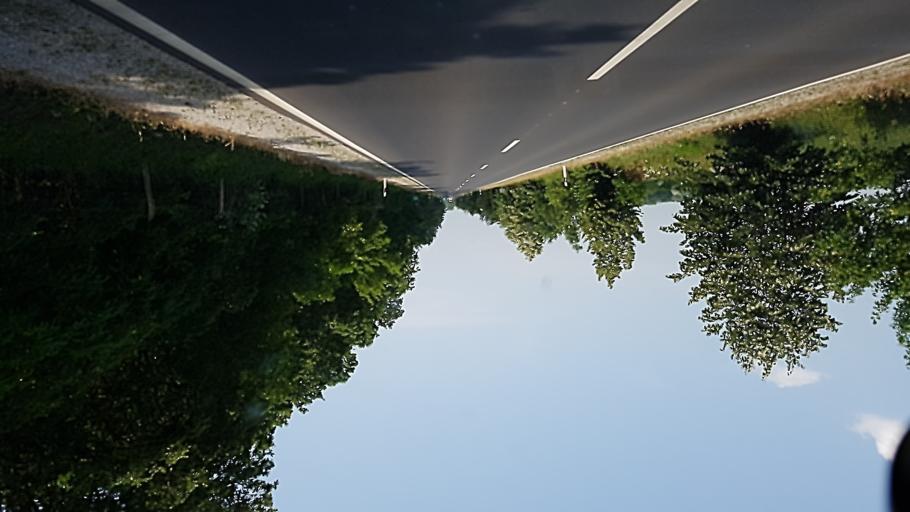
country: HU
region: Heves
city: Besenyotelek
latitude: 47.6759
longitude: 20.5257
